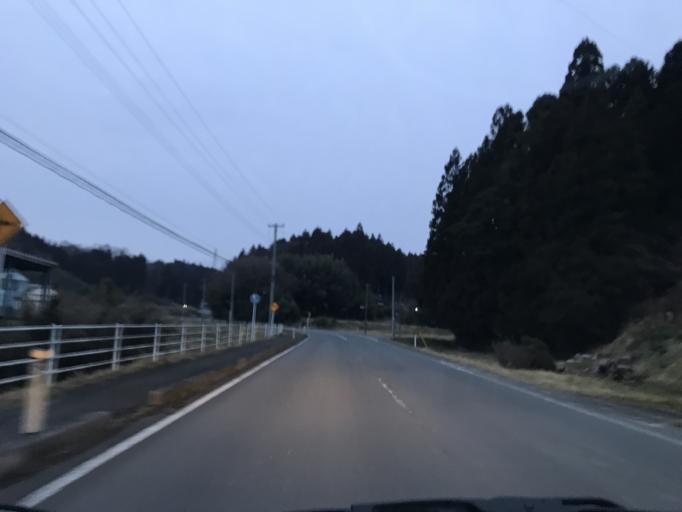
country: JP
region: Iwate
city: Ichinoseki
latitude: 38.8103
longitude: 141.1175
